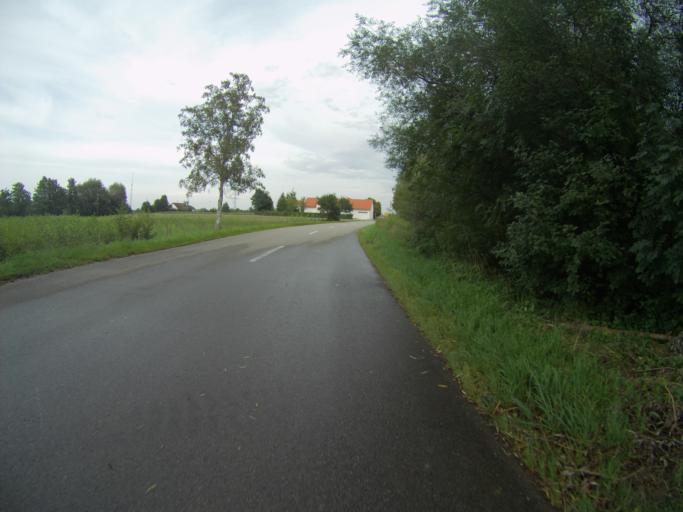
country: DE
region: Bavaria
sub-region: Upper Bavaria
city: Marzling
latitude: 48.3864
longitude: 11.8168
